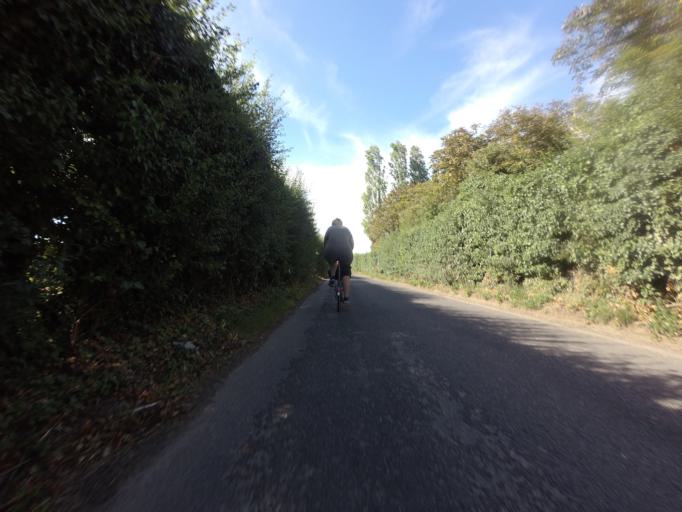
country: GB
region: England
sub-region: Kent
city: Birchington-on-Sea
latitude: 51.3458
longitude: 1.2617
